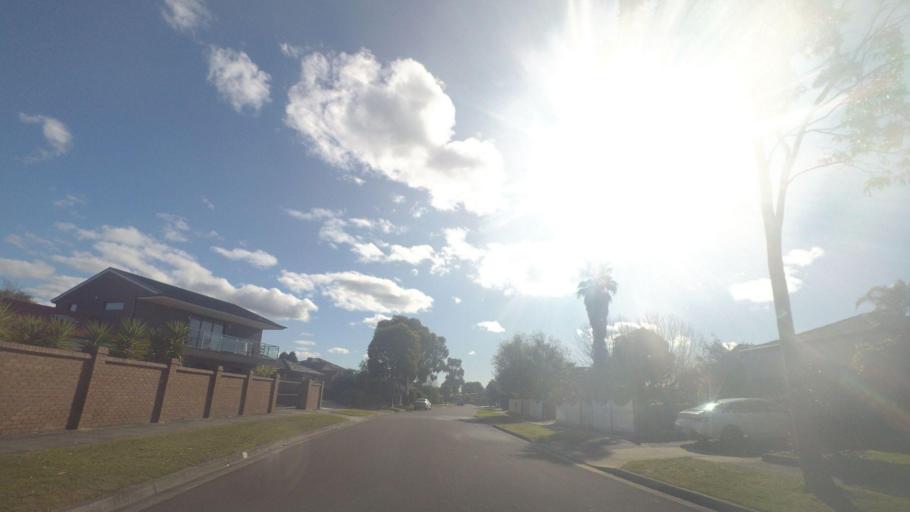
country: AU
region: Victoria
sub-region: Knox
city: Knoxfield
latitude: -37.9149
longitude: 145.2546
